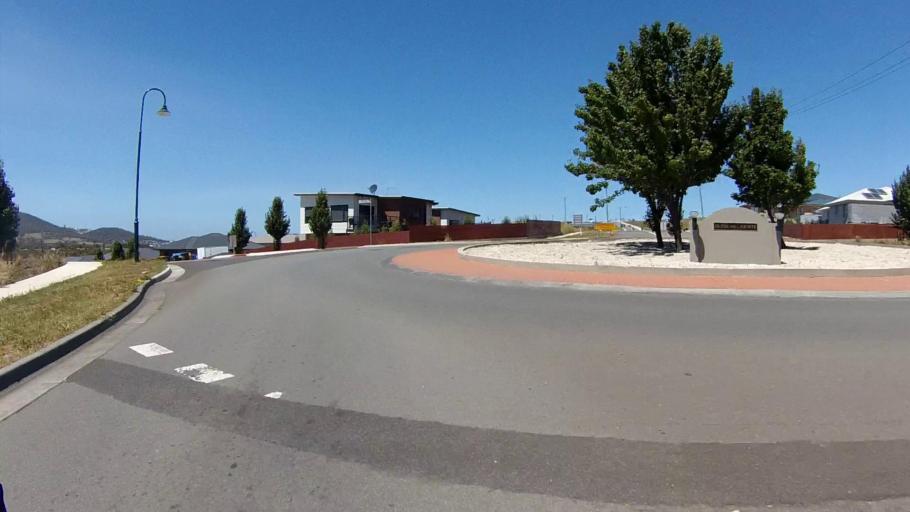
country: AU
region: Tasmania
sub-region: Clarence
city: Howrah
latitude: -42.8837
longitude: 147.4284
